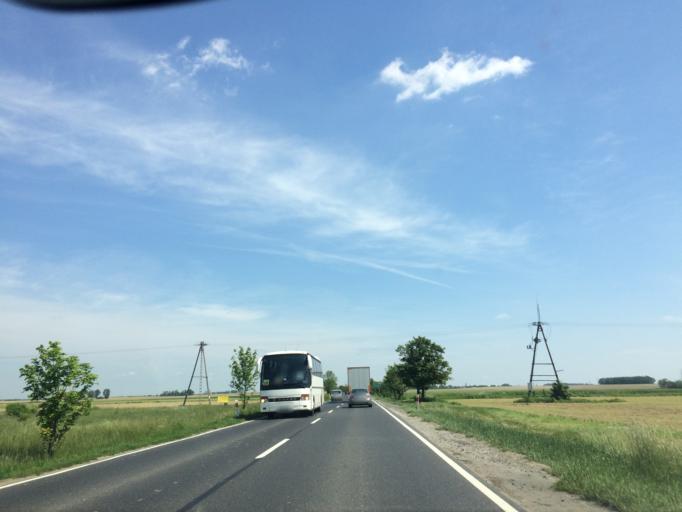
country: PL
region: Lower Silesian Voivodeship
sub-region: Powiat wroclawski
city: Gniechowice
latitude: 50.9923
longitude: 16.8419
